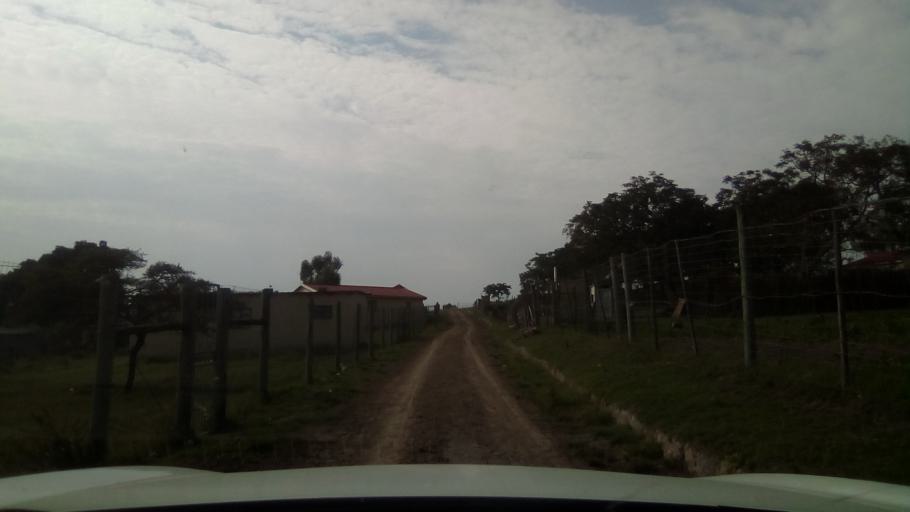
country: ZA
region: Eastern Cape
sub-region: Buffalo City Metropolitan Municipality
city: Bhisho
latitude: -33.0053
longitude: 27.3003
